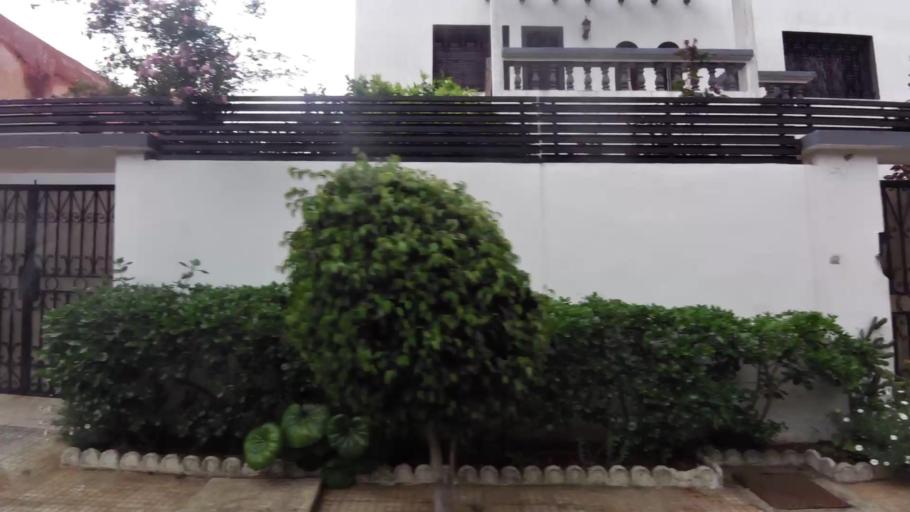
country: MA
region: Grand Casablanca
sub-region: Casablanca
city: Casablanca
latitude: 33.5772
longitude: -7.6613
